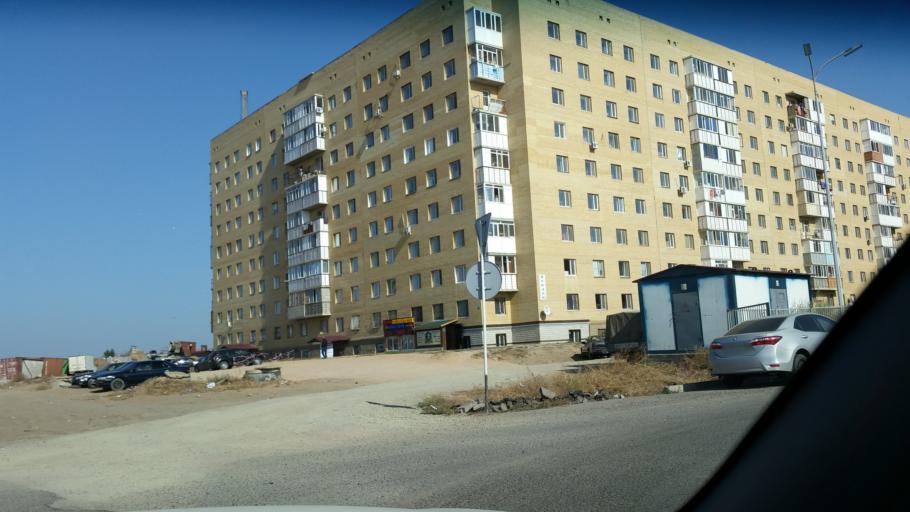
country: KZ
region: Astana Qalasy
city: Astana
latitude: 51.1731
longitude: 71.3782
